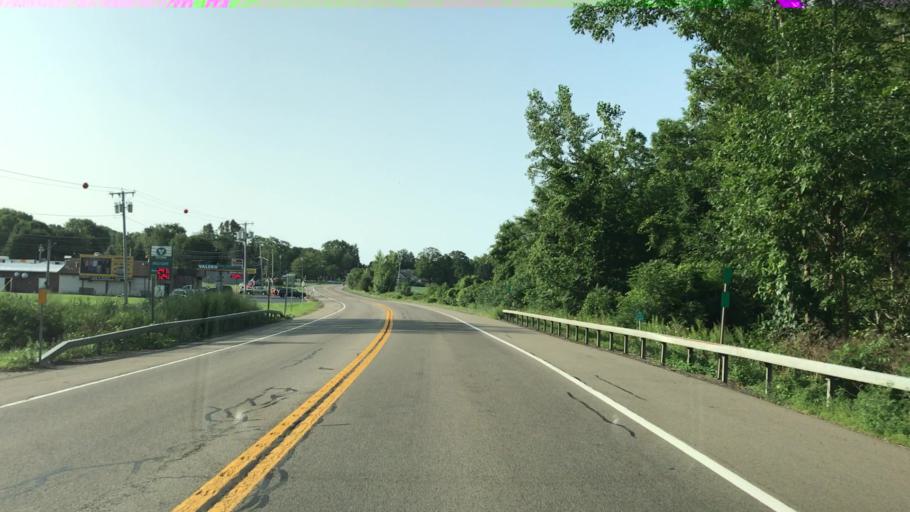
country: US
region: New York
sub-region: Chautauqua County
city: Fredonia
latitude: 42.3526
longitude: -79.3119
